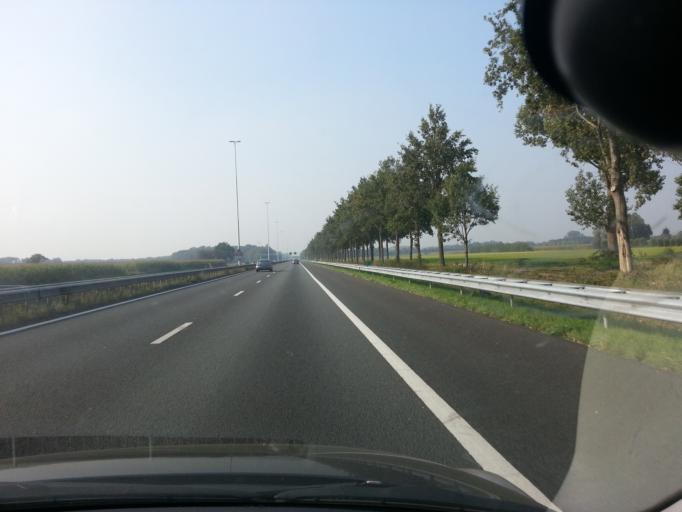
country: NL
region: North Brabant
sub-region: Gemeente Oirschot
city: Oirschot
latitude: 51.5049
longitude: 5.2859
